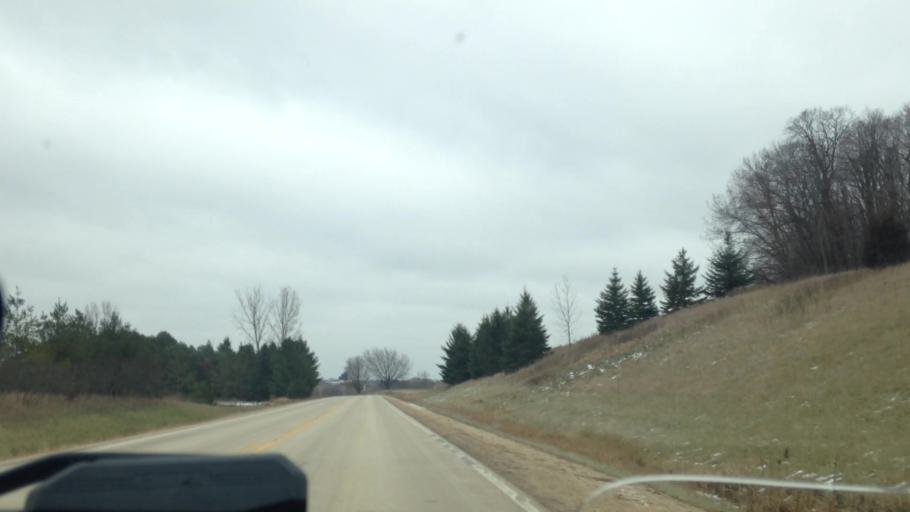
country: US
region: Wisconsin
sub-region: Dodge County
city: Mayville
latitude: 43.4814
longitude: -88.5079
